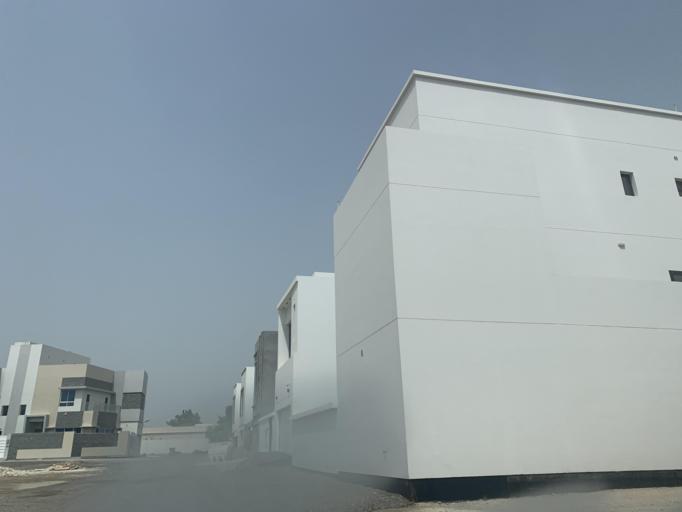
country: BH
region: Manama
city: Jidd Hafs
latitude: 26.1986
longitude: 50.4684
